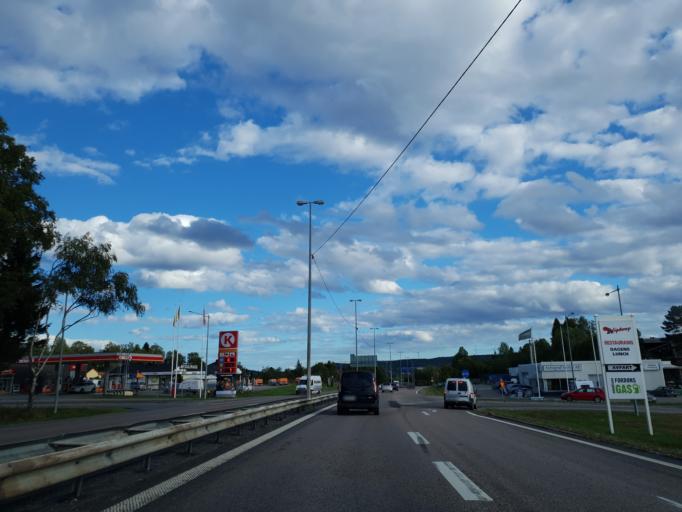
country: SE
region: Vaesternorrland
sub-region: Haernoesands Kommun
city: Haernoesand
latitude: 62.6436
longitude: 17.9092
